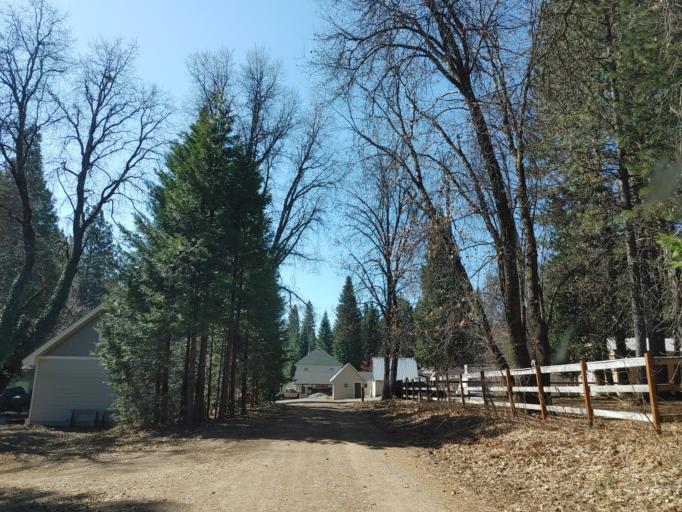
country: US
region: California
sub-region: Siskiyou County
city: McCloud
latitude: 41.2585
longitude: -122.1425
